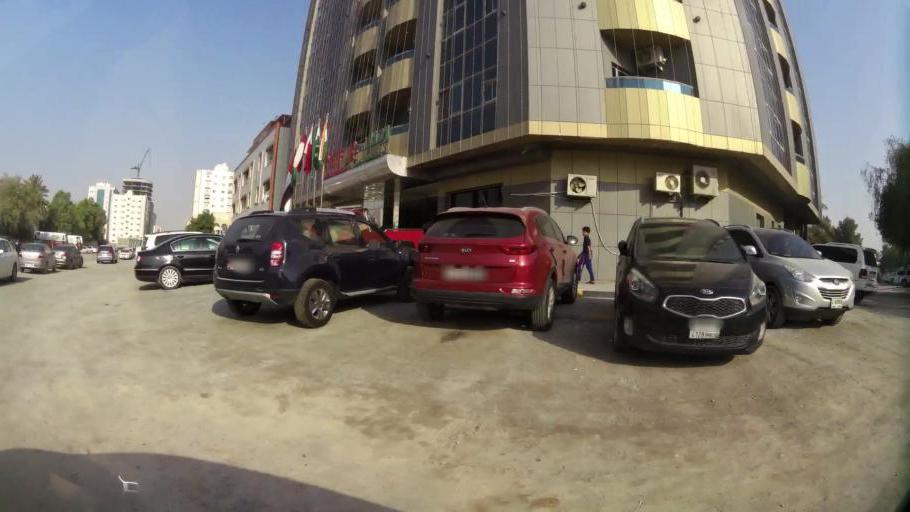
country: AE
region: Ajman
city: Ajman
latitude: 25.3879
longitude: 55.4433
